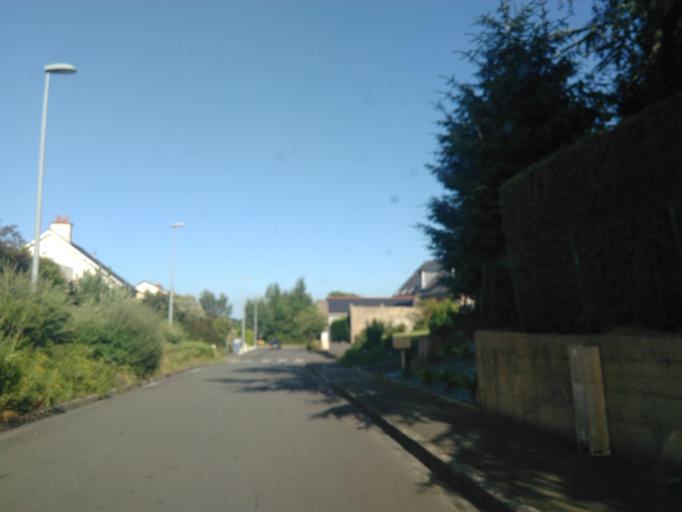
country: FR
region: Brittany
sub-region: Departement d'Ille-et-Vilaine
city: Pleumeleuc
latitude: 48.1858
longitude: -1.9206
